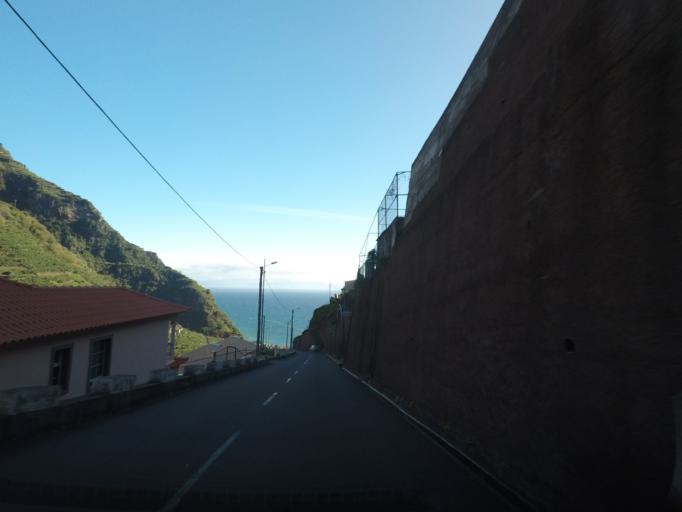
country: PT
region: Madeira
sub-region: Calheta
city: Arco da Calheta
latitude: 32.7081
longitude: -17.1350
